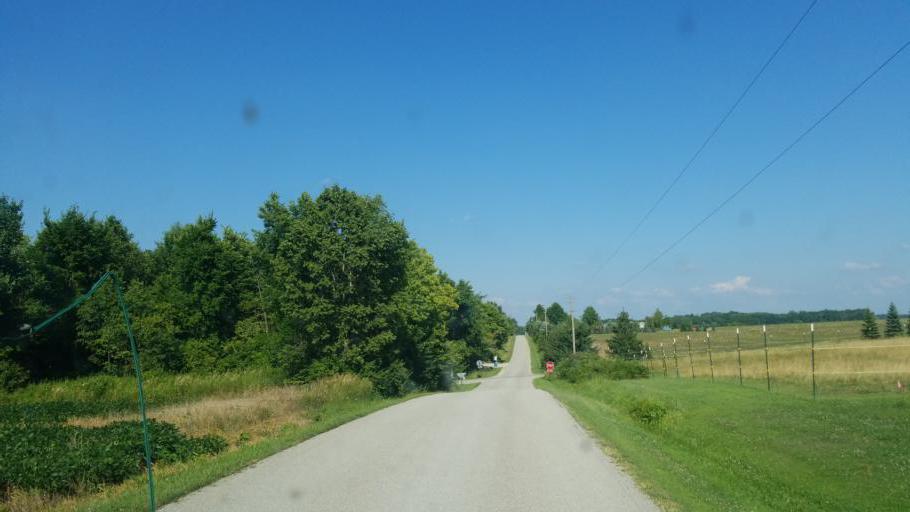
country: US
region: Ohio
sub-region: Wyandot County
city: Upper Sandusky
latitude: 40.7884
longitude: -83.3534
